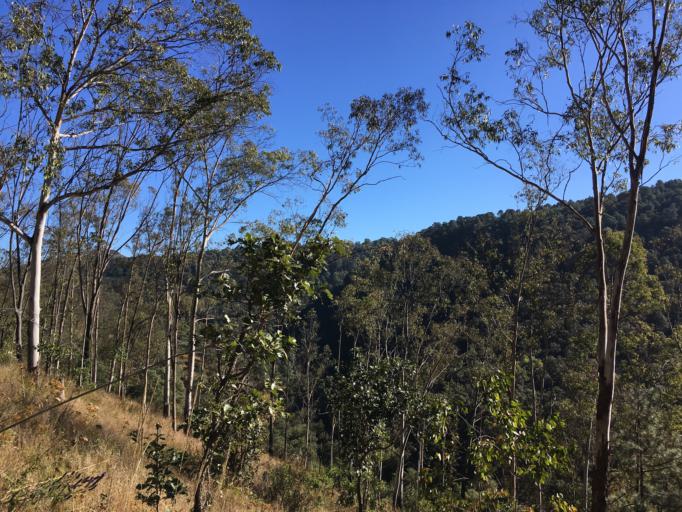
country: MX
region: Michoacan
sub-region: Morelia
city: Montana Monarca (Punta Altozano)
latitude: 19.6596
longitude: -101.1453
